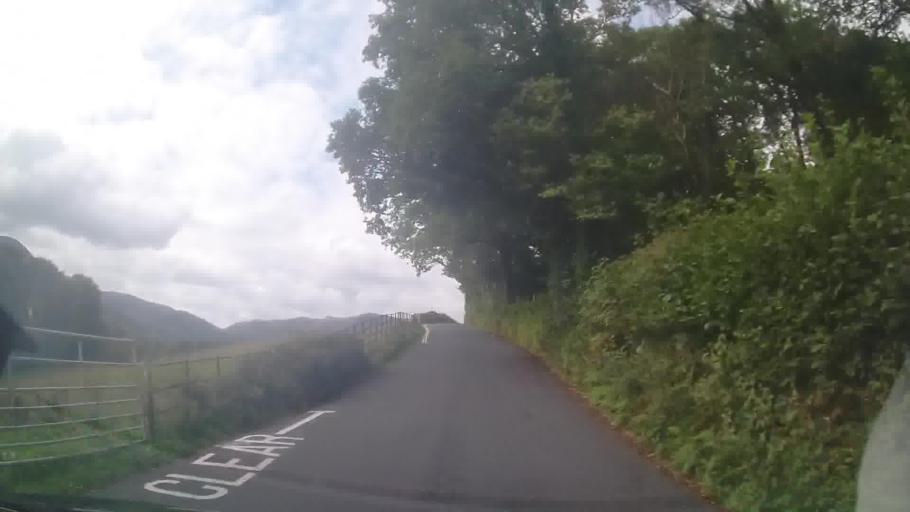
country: GB
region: England
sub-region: Cumbria
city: Ambleside
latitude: 54.4189
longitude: -3.0476
